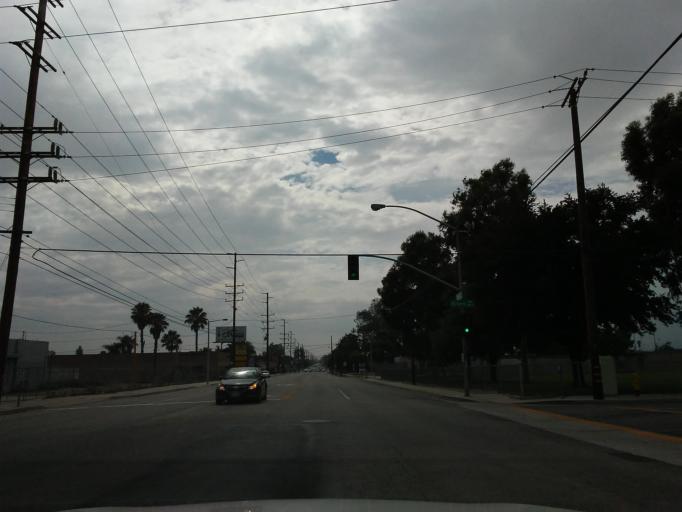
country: US
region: California
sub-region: San Bernardino County
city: San Bernardino
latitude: 34.0922
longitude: -117.2849
